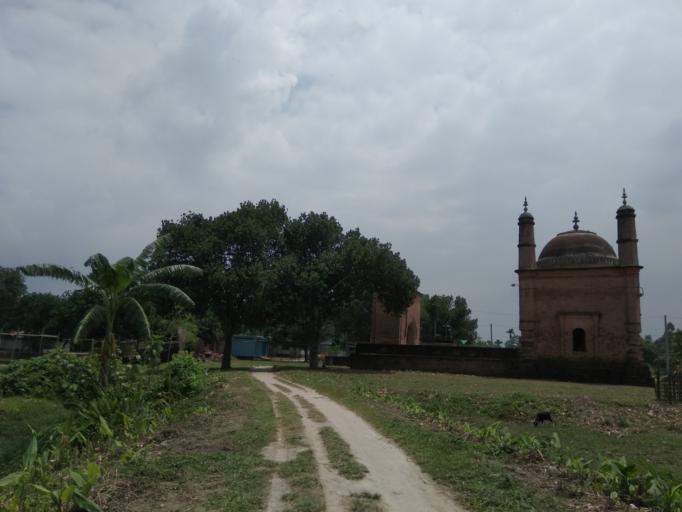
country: BD
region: Rangpur Division
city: Thakurgaon
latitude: 26.1257
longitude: 88.5639
